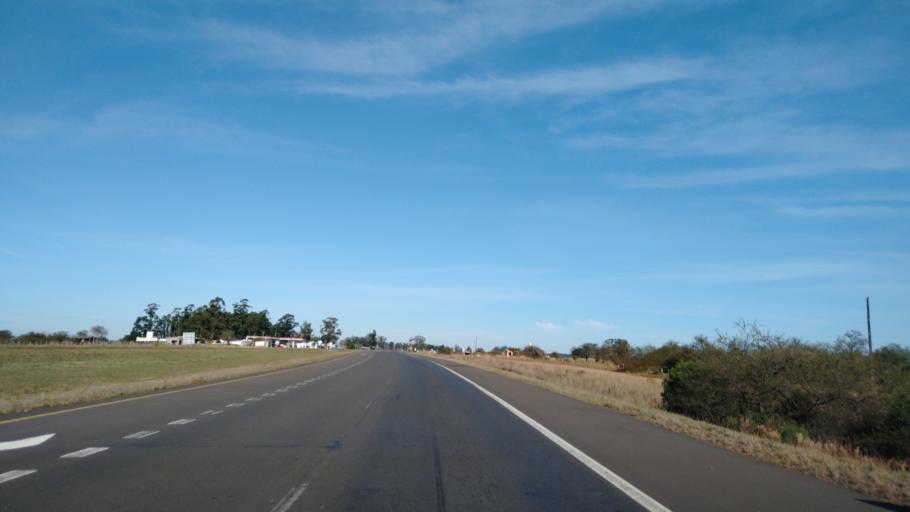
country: AR
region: Corrientes
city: Libertad
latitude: -30.0271
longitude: -57.7533
